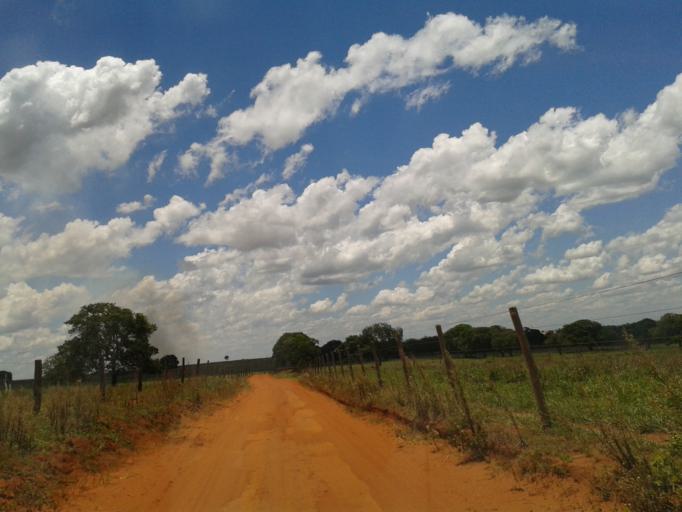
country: BR
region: Minas Gerais
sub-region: Centralina
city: Centralina
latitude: -18.7075
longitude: -49.1734
